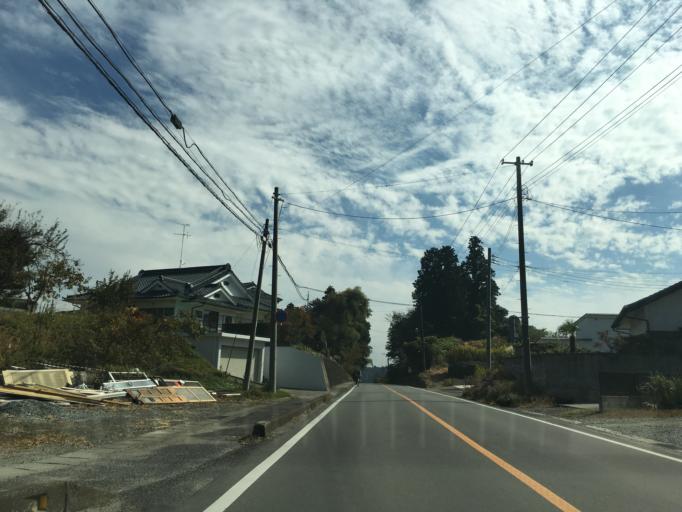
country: JP
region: Fukushima
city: Sukagawa
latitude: 37.2811
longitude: 140.3924
